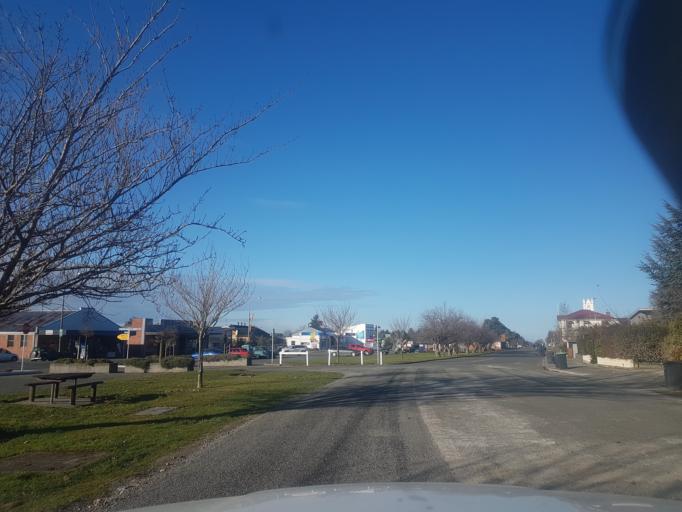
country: NZ
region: Canterbury
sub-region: Timaru District
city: Pleasant Point
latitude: -44.2605
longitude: 171.1287
